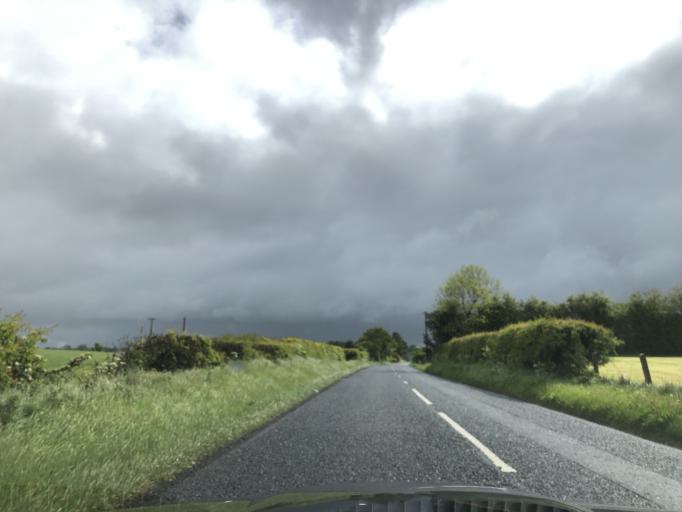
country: GB
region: Northern Ireland
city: Bushmills
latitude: 55.1590
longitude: -6.3921
